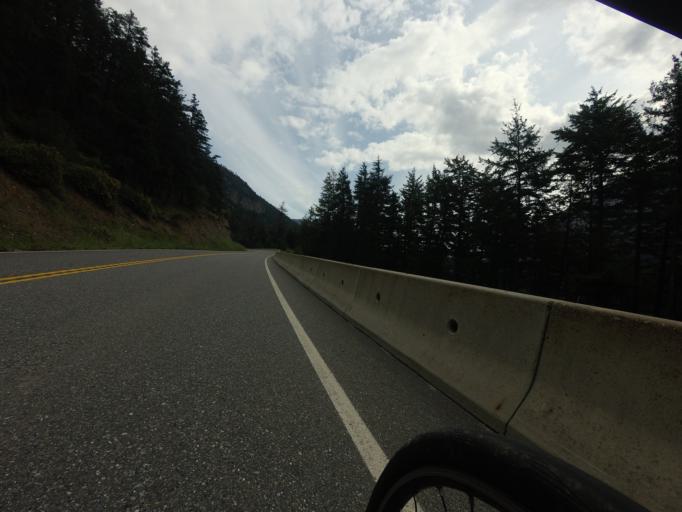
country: CA
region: British Columbia
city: Lillooet
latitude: 50.6450
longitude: -122.0230
